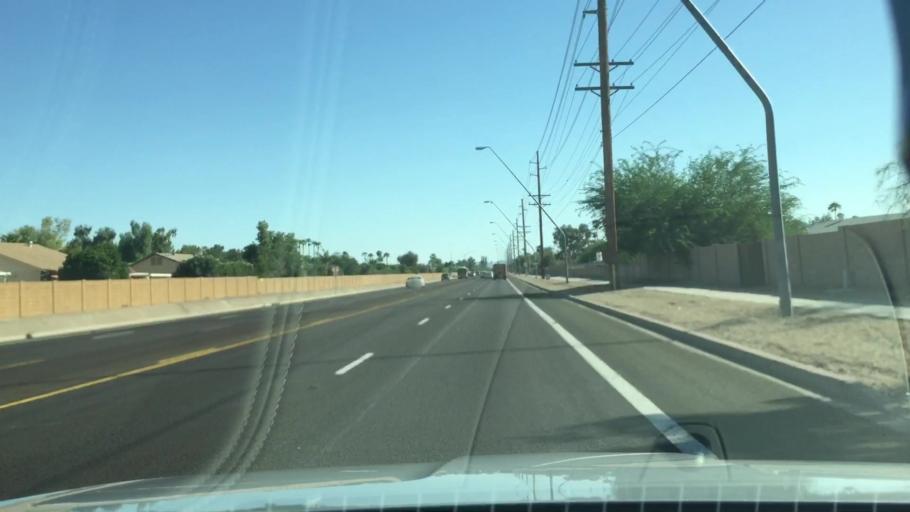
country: US
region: Arizona
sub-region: Pinal County
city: Apache Junction
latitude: 33.4051
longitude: -111.6676
